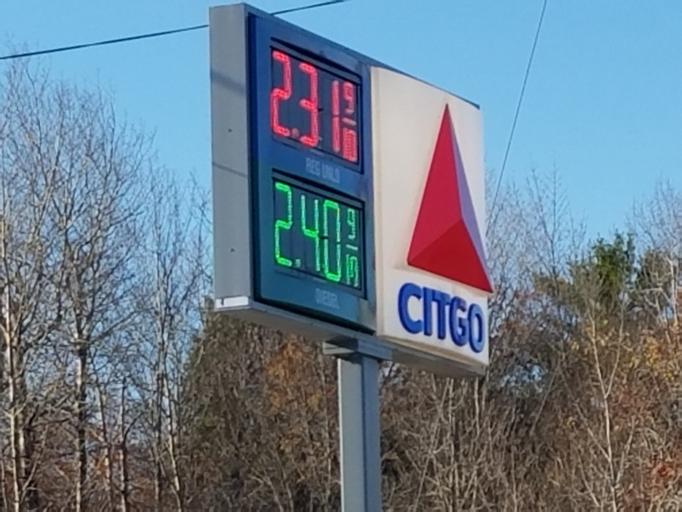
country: US
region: Maine
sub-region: Penobscot County
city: Hermon
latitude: 44.7572
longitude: -68.9733
